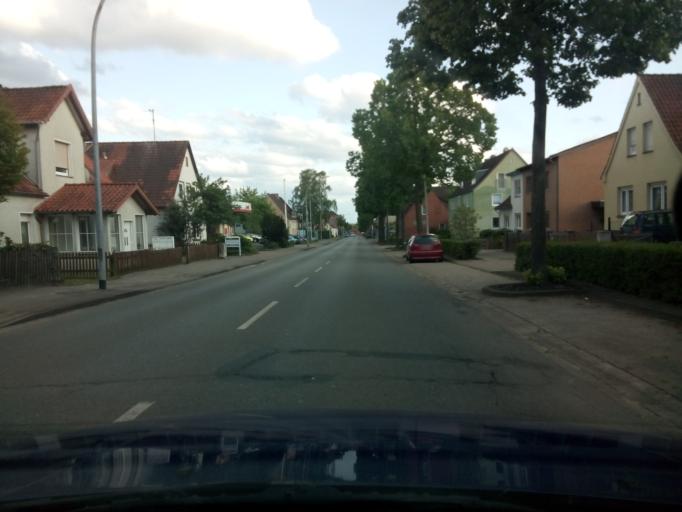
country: DE
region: Lower Saxony
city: Walsrode
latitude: 52.8687
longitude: 9.5852
